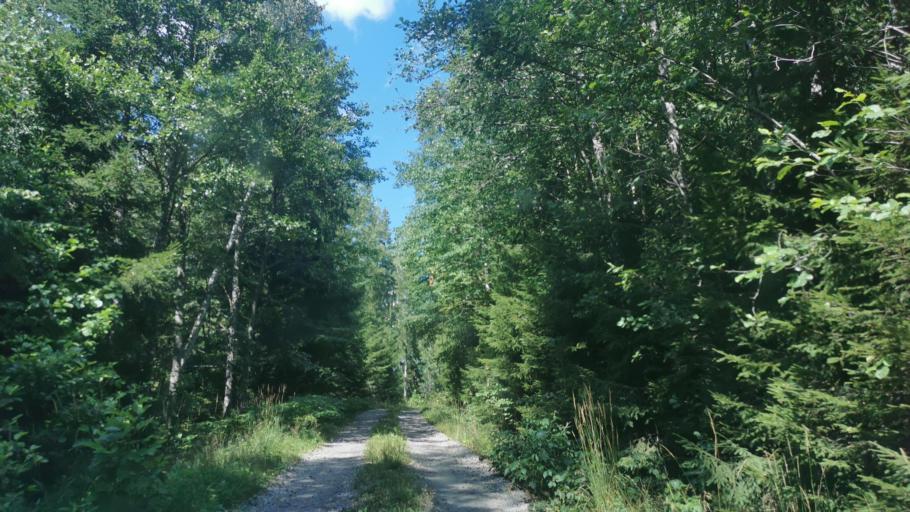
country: SE
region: OEstergoetland
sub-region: Finspangs Kommun
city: Finspang
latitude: 58.7998
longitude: 15.8101
